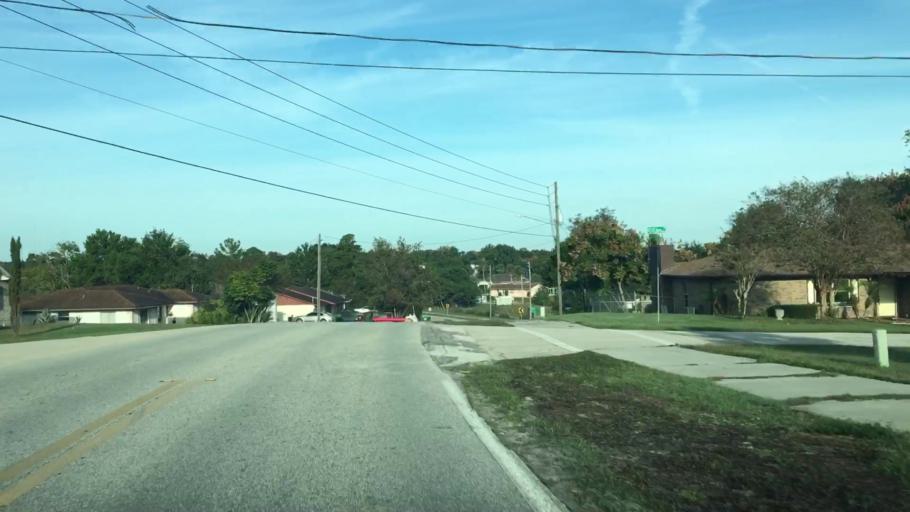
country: US
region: Florida
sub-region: Volusia County
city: Deltona
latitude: 28.9171
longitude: -81.2302
